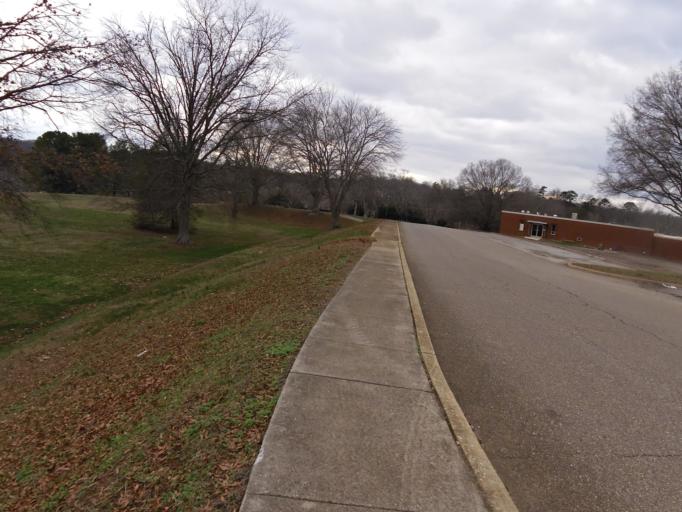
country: US
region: Tennessee
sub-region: Knox County
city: Knoxville
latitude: 35.9198
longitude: -83.9940
